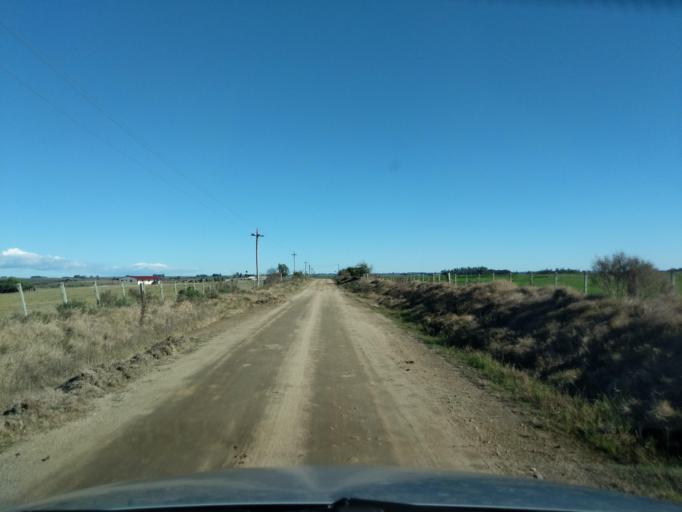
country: UY
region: Florida
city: Florida
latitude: -34.0821
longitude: -56.2517
